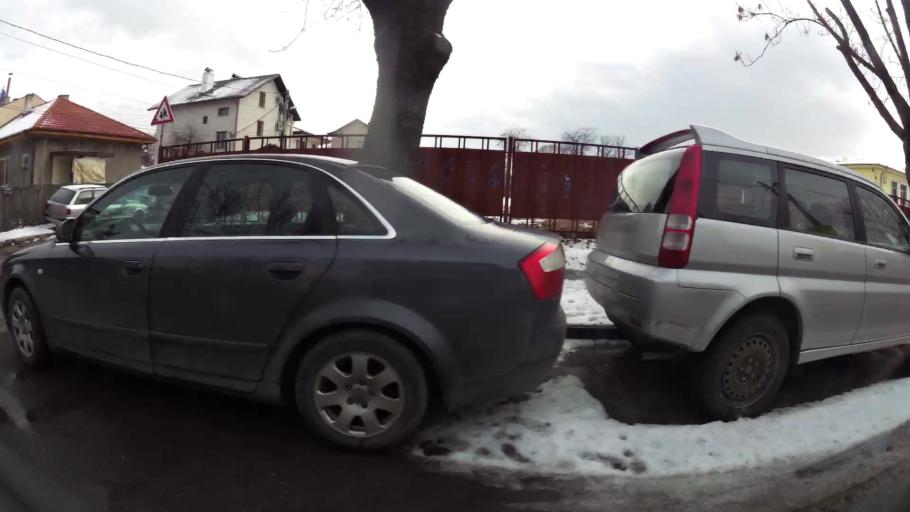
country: BG
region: Sofia-Capital
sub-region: Stolichna Obshtina
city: Sofia
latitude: 42.7043
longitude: 23.3789
